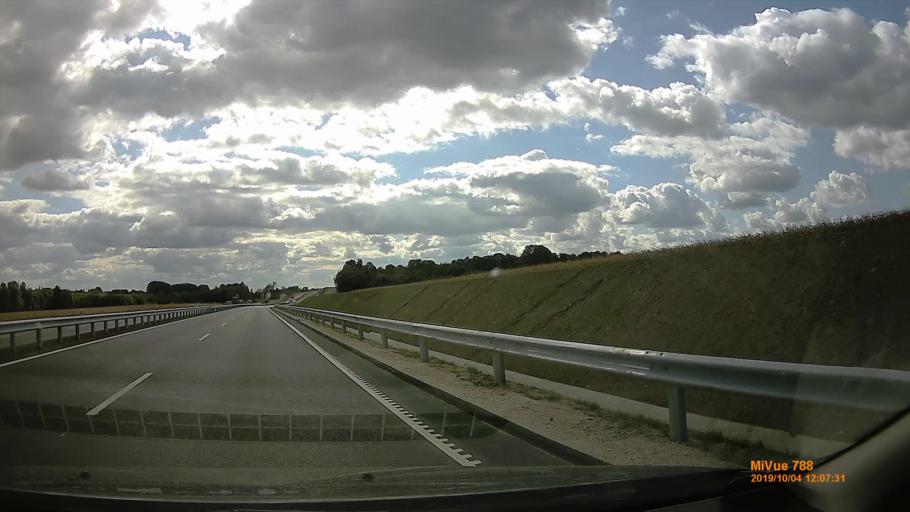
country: HU
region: Somogy
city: Karad
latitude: 46.5400
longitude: 17.8159
